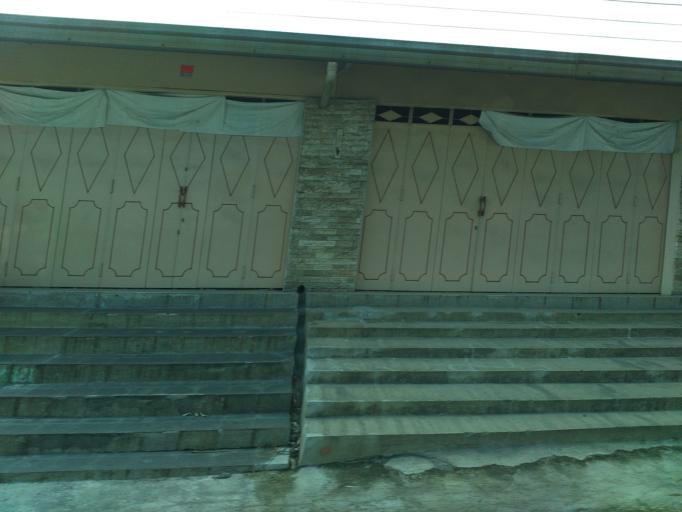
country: ID
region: Central Java
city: Ceper
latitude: -7.6652
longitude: 110.6654
